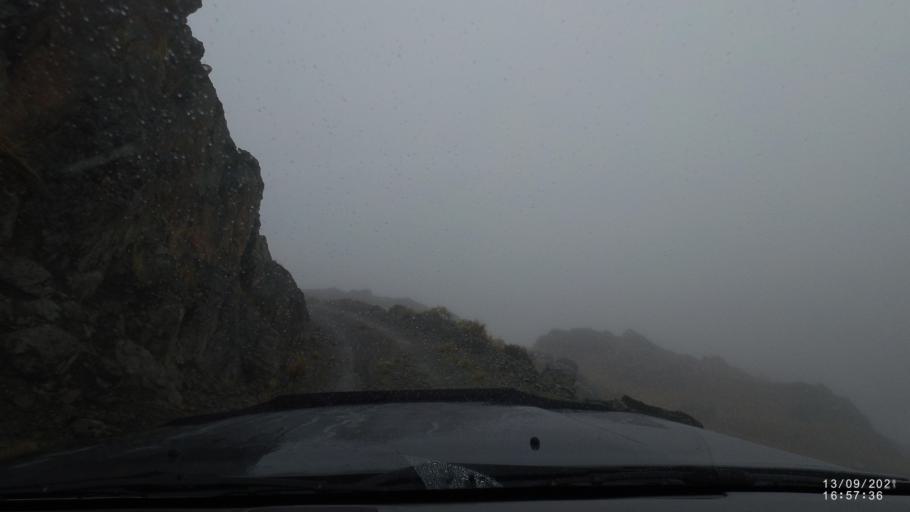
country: BO
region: Cochabamba
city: Colomi
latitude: -17.3060
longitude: -65.7159
